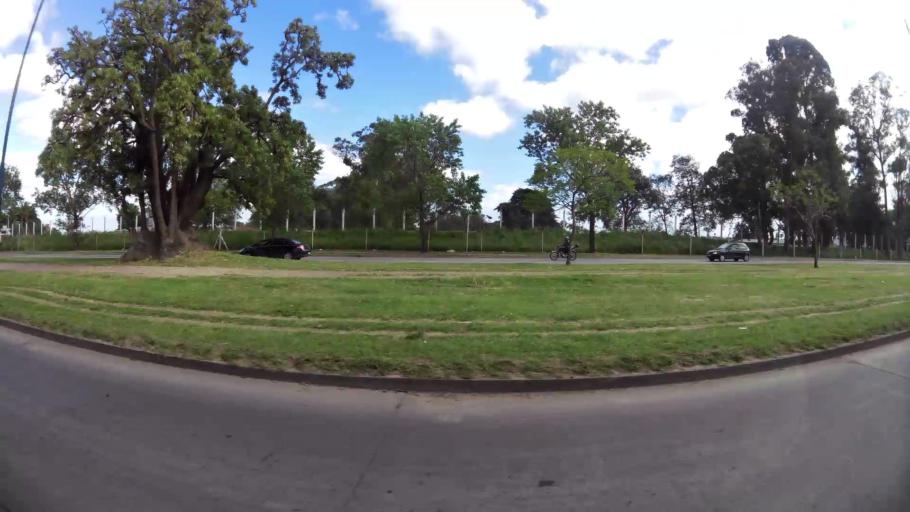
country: UY
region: Montevideo
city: Montevideo
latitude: -34.8664
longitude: -56.1580
